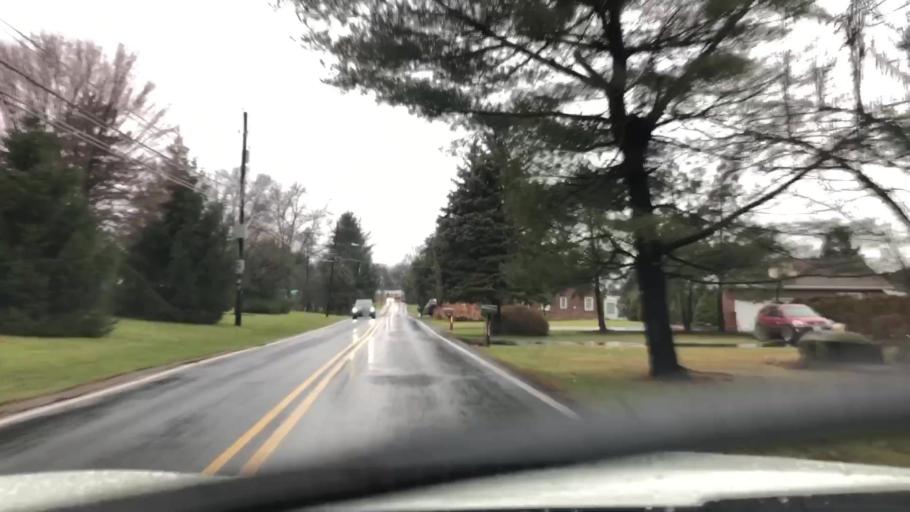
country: US
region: Pennsylvania
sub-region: Lehigh County
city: Dorneyville
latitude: 40.5617
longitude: -75.5285
